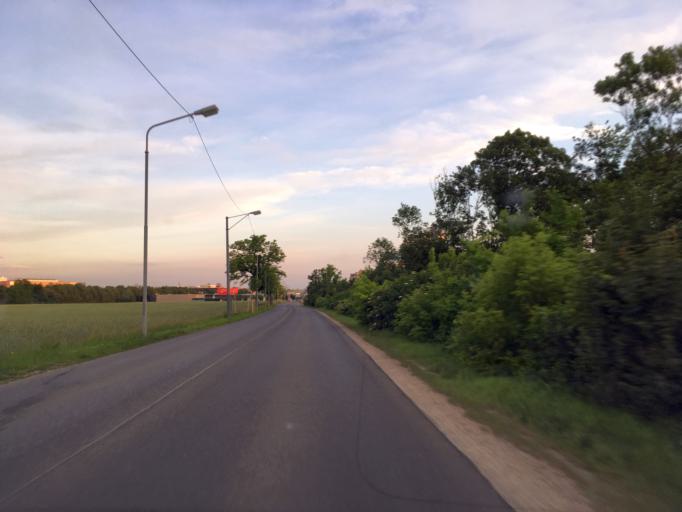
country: AT
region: Lower Austria
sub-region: Politischer Bezirk Wien-Umgebung
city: Gerasdorf bei Wien
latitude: 48.2713
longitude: 16.4567
